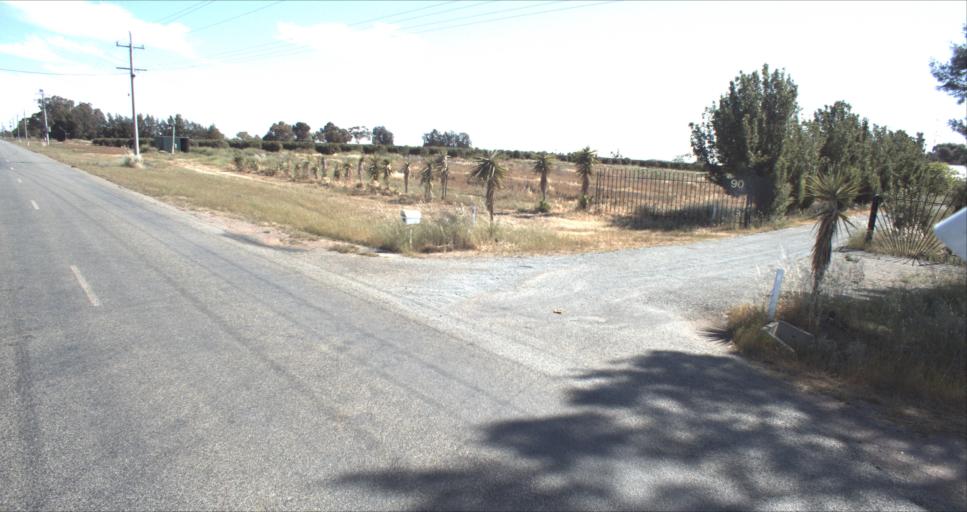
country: AU
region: New South Wales
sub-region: Leeton
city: Leeton
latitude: -34.5595
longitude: 146.3838
